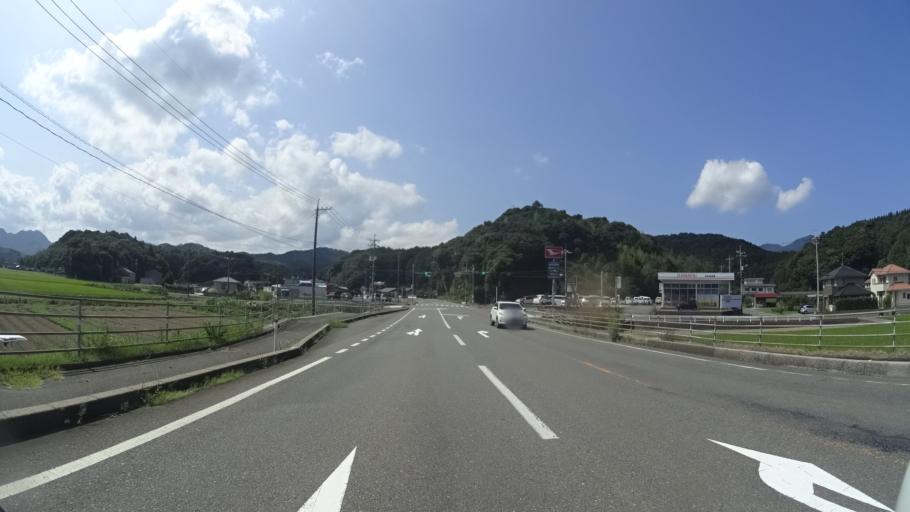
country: JP
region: Shimane
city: Masuda
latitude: 34.6461
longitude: 131.6628
